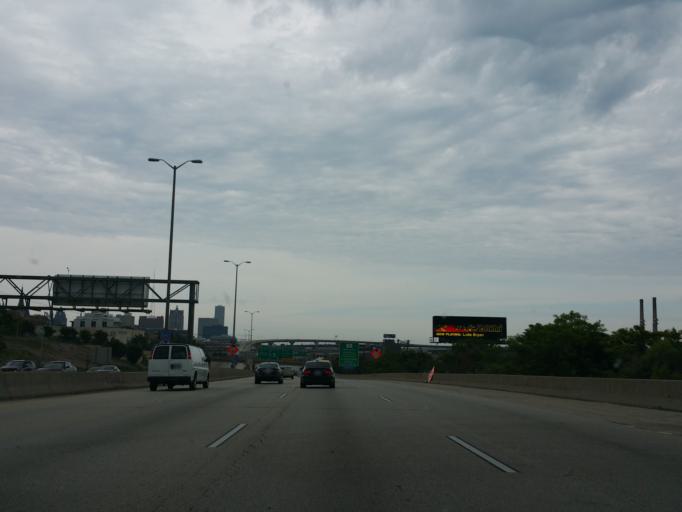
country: US
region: Wisconsin
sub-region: Milwaukee County
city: Milwaukee
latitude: 43.0354
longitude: -87.9388
